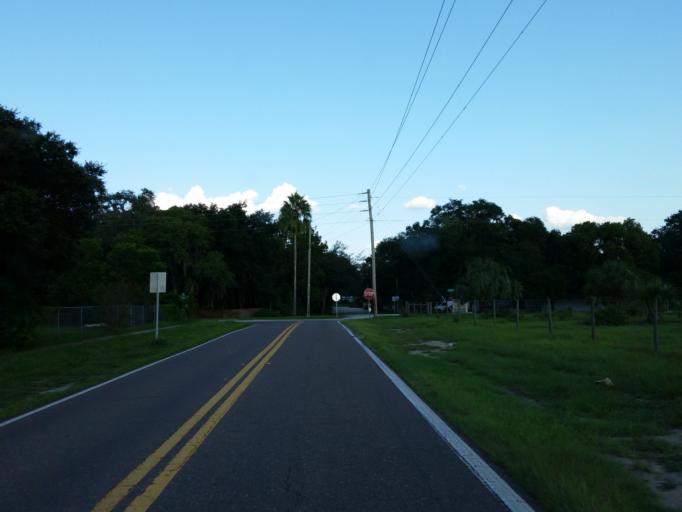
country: US
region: Florida
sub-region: Hillsborough County
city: Bloomingdale
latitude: 27.9083
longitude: -82.2536
